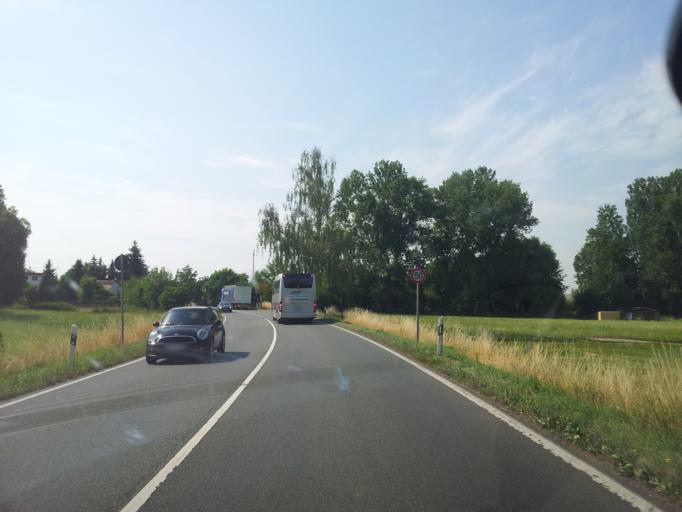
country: DE
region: Saxony
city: Stauchitz
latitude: 51.2675
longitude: 13.2580
